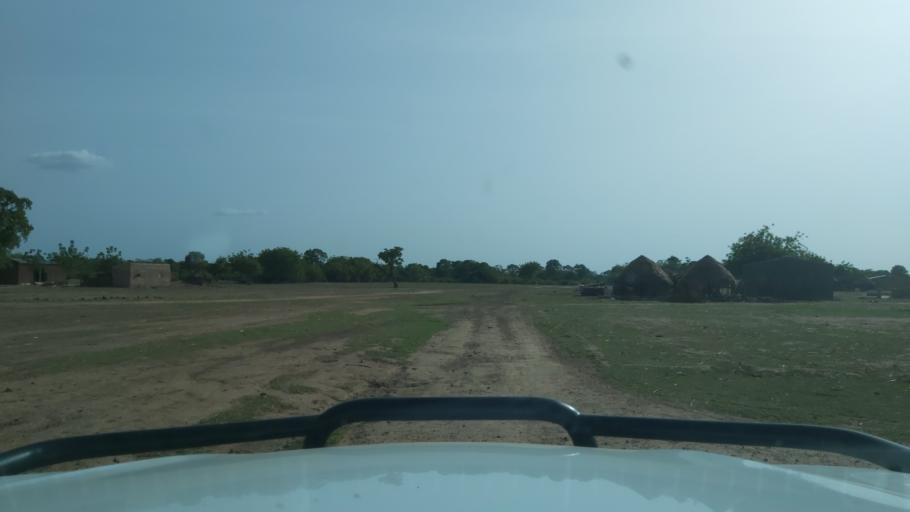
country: ML
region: Koulikoro
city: Koulikoro
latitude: 13.1648
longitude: -7.7941
